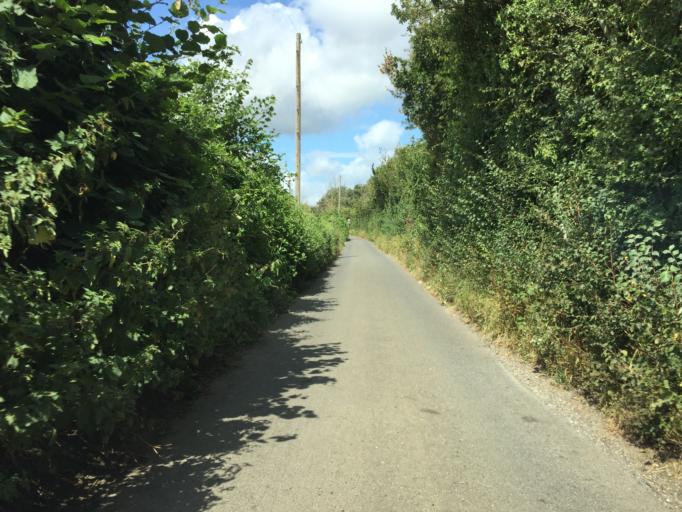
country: GB
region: England
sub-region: Kent
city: West Malling
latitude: 51.2977
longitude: 0.3969
